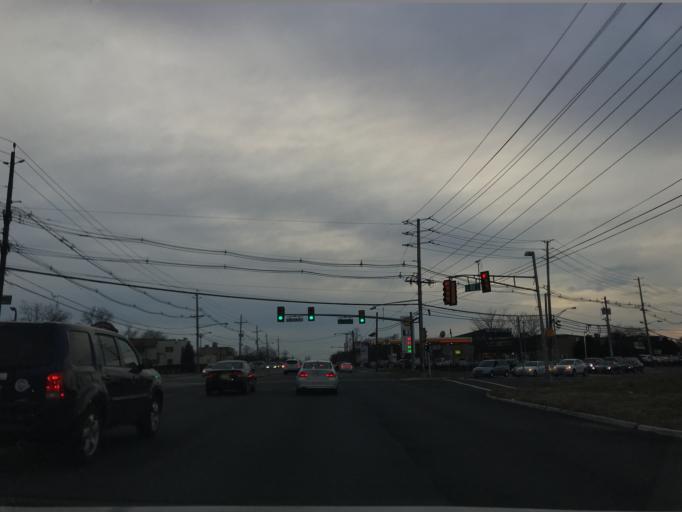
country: US
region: New Jersey
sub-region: Middlesex County
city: Piscataway
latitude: 40.5154
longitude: -74.3746
